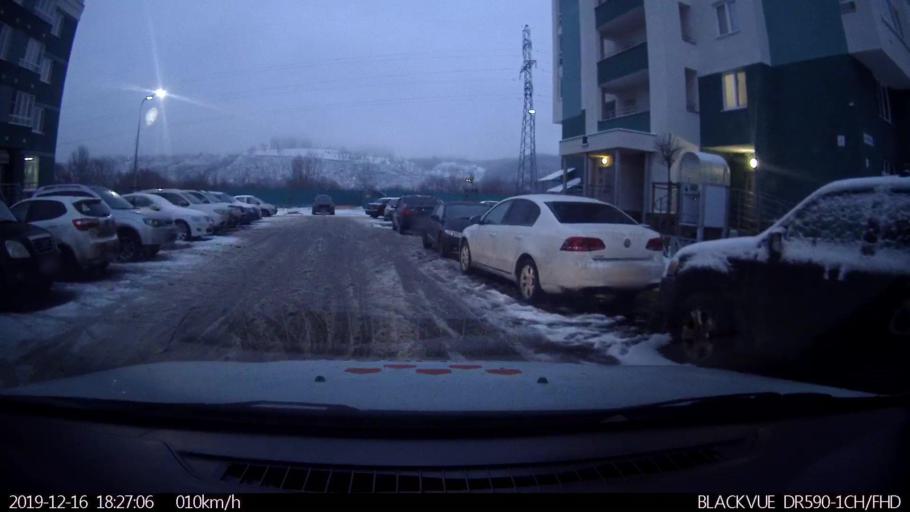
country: RU
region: Nizjnij Novgorod
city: Nizhniy Novgorod
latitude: 56.3016
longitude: 43.9529
